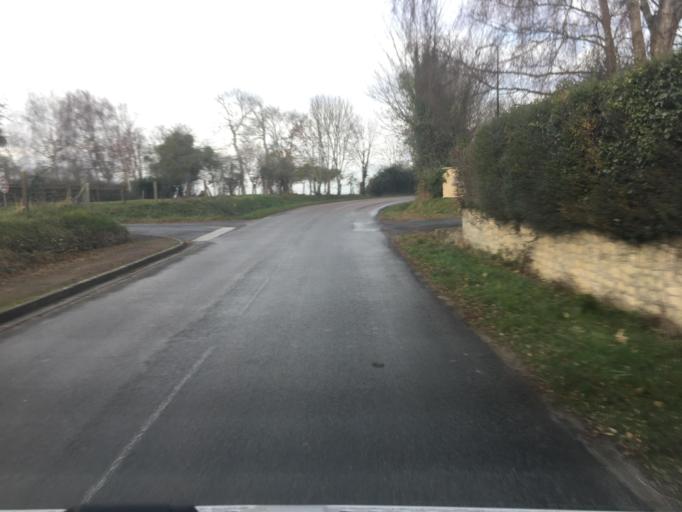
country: FR
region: Lower Normandy
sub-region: Departement du Calvados
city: Ver-sur-Mer
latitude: 49.3164
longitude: -0.5517
